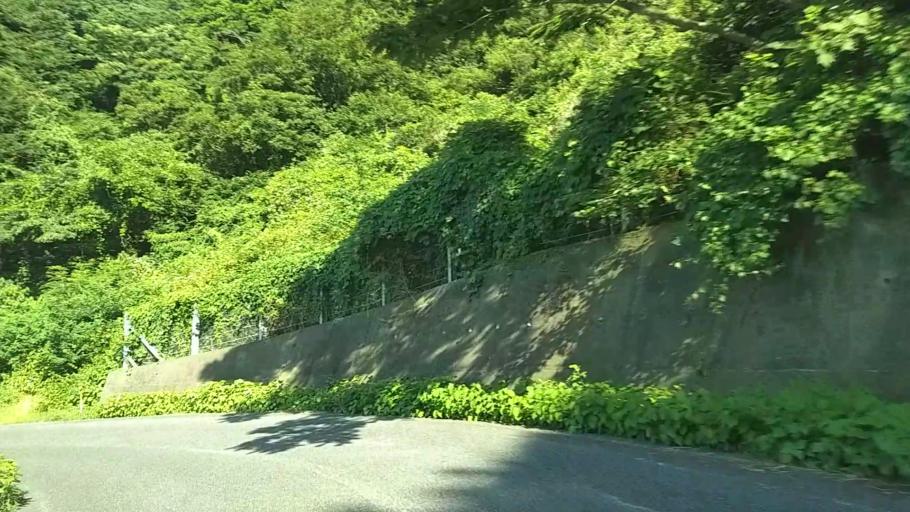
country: JP
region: Shizuoka
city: Shimoda
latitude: 34.7313
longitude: 138.7499
